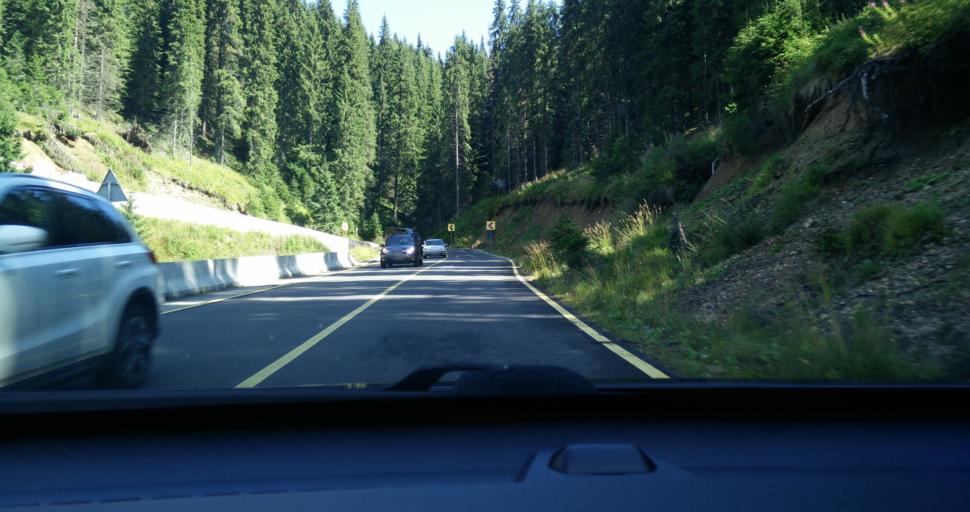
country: RO
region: Hunedoara
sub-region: Oras Petrila
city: Petrila
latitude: 45.4502
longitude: 23.6199
